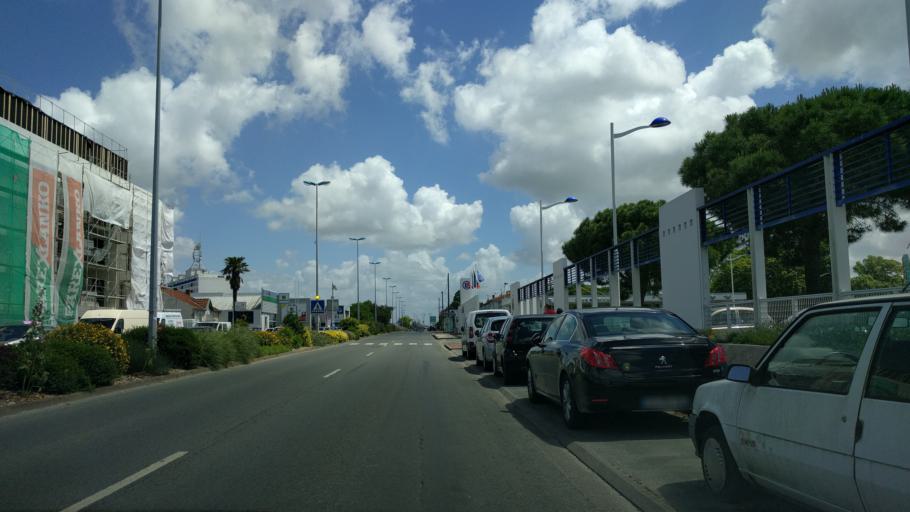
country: FR
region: Poitou-Charentes
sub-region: Departement de la Charente-Maritime
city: Puilboreau
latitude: 46.1697
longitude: -1.1273
